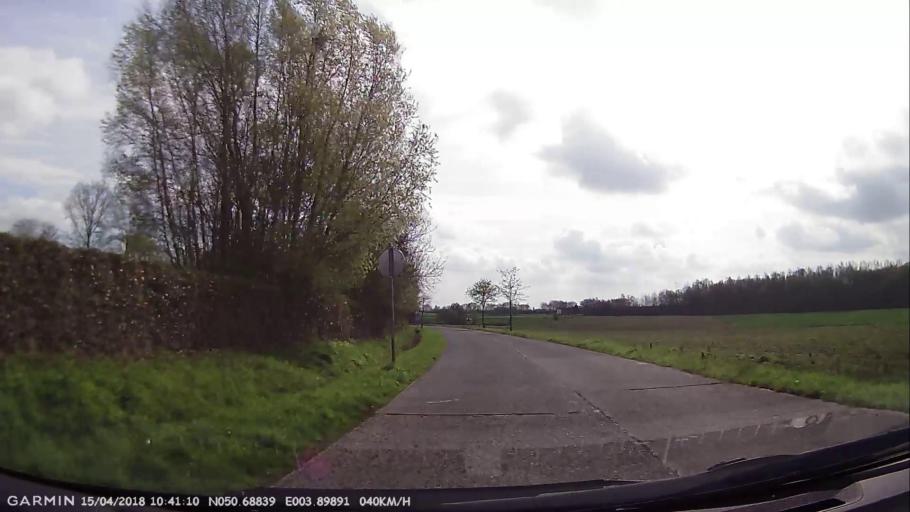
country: BE
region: Wallonia
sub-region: Province du Hainaut
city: Silly
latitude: 50.6884
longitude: 3.8989
